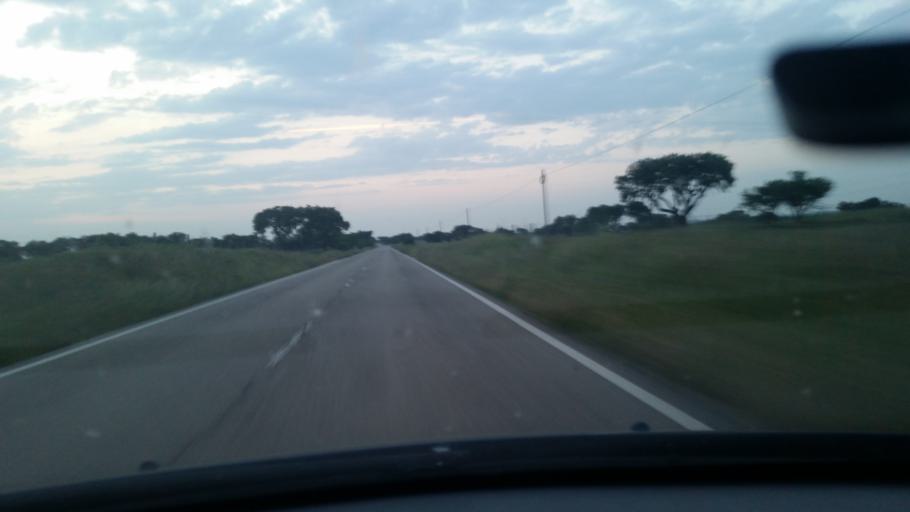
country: PT
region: Evora
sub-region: Arraiolos
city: Arraiolos
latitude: 38.8339
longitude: -8.0095
